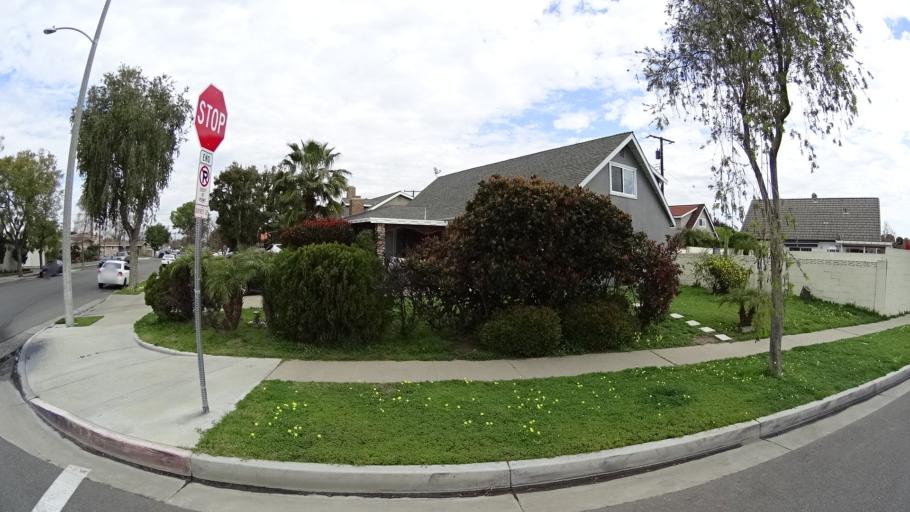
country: US
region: California
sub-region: Orange County
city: Anaheim
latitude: 33.8405
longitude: -117.8847
